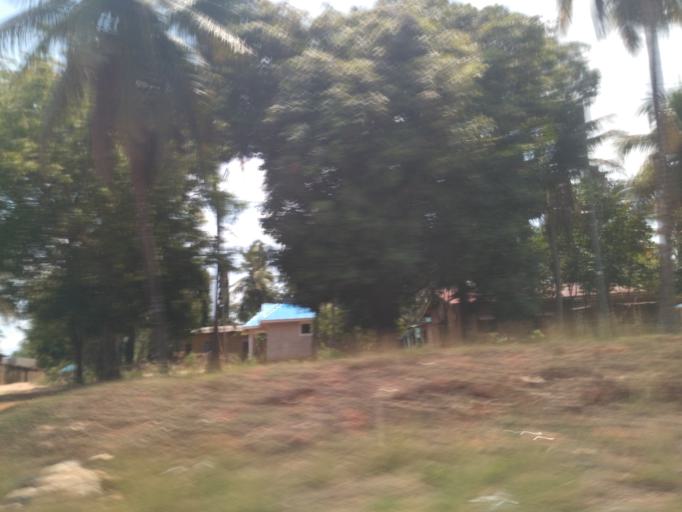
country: TZ
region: Dar es Salaam
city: Dar es Salaam
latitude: -6.8390
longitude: 39.3492
